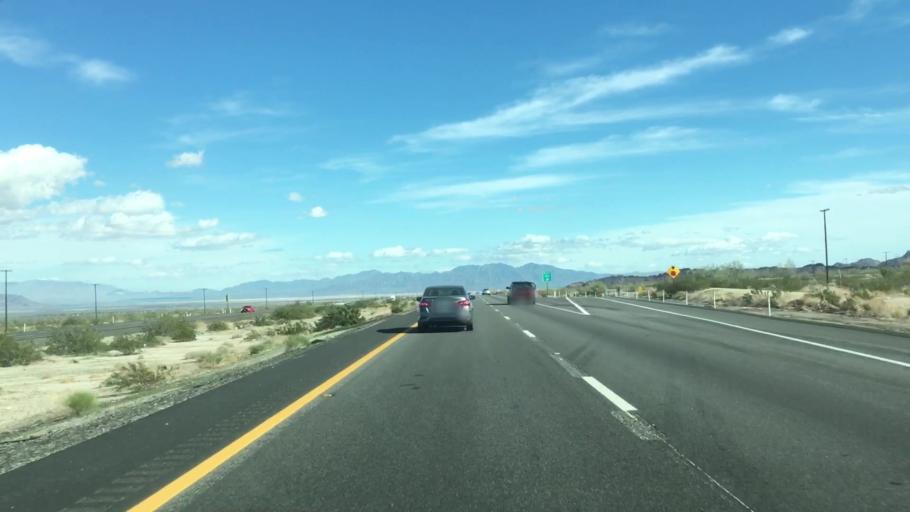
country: US
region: California
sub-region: Imperial County
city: Niland
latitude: 33.7012
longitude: -115.4555
